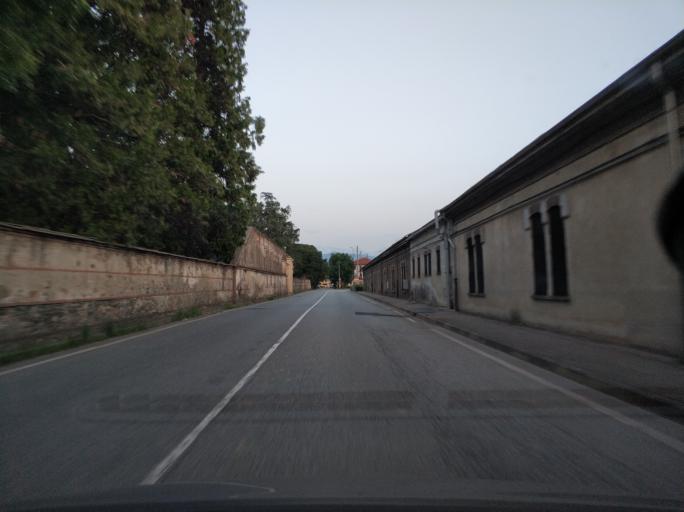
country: IT
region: Piedmont
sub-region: Provincia di Torino
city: San Maurizio
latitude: 45.2186
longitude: 7.6377
